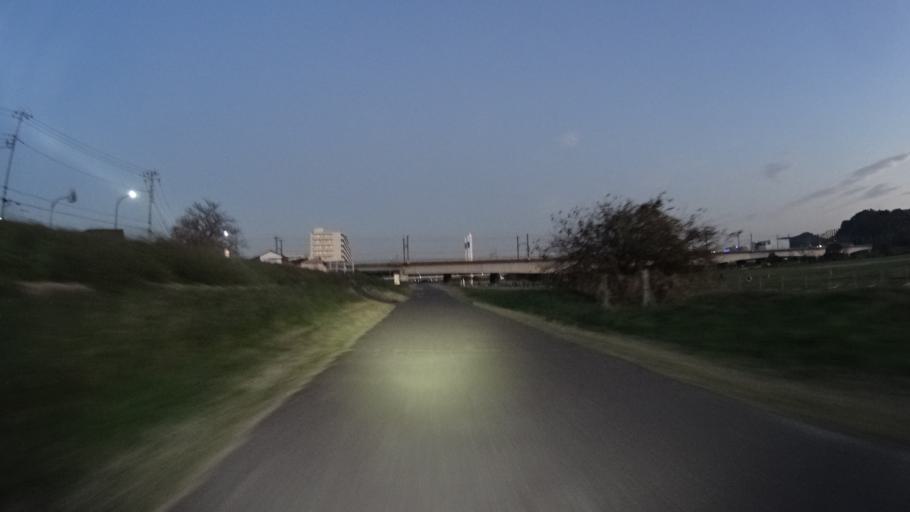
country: JP
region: Tokyo
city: Kokubunji
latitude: 35.6550
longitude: 139.4812
